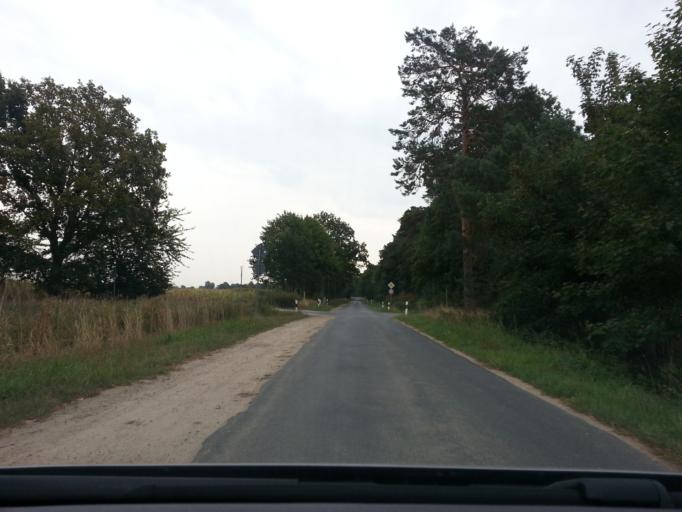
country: DE
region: Mecklenburg-Vorpommern
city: Ferdinandshof
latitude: 53.6589
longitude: 13.9175
